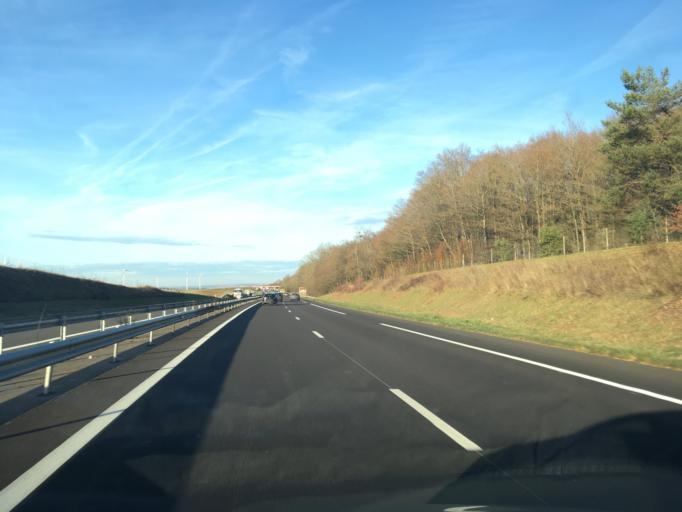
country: FR
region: Bourgogne
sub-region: Departement de l'Yonne
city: Joux-la-Ville
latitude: 47.6056
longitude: 3.9095
